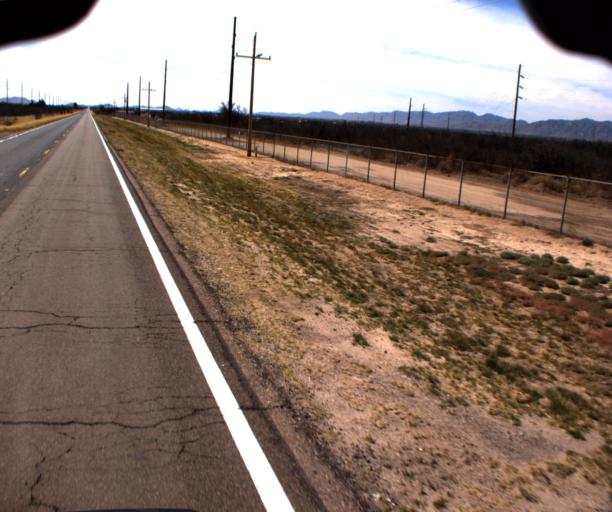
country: US
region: Arizona
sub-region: Cochise County
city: Willcox
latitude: 32.0575
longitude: -109.8899
